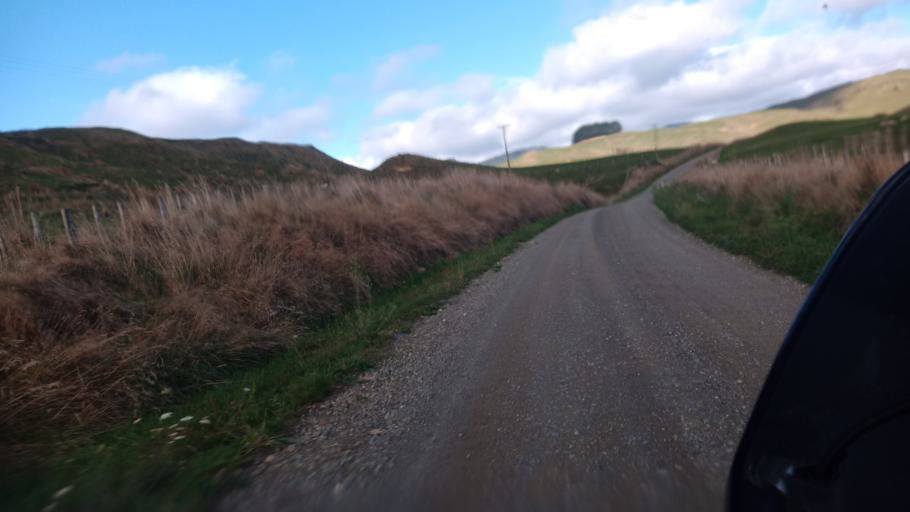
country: NZ
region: Bay of Plenty
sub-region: Opotiki District
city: Opotiki
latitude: -38.4562
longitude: 177.3928
